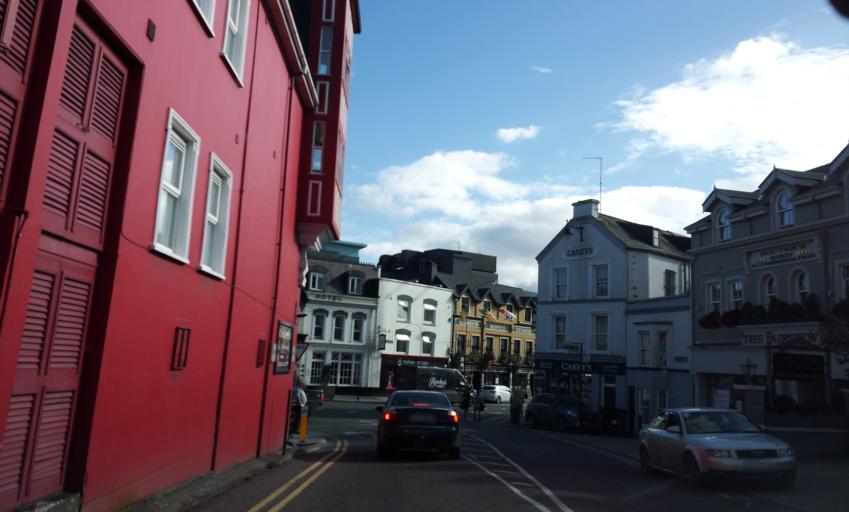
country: IE
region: Munster
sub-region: Ciarrai
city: Cill Airne
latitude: 52.0602
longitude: -9.5061
